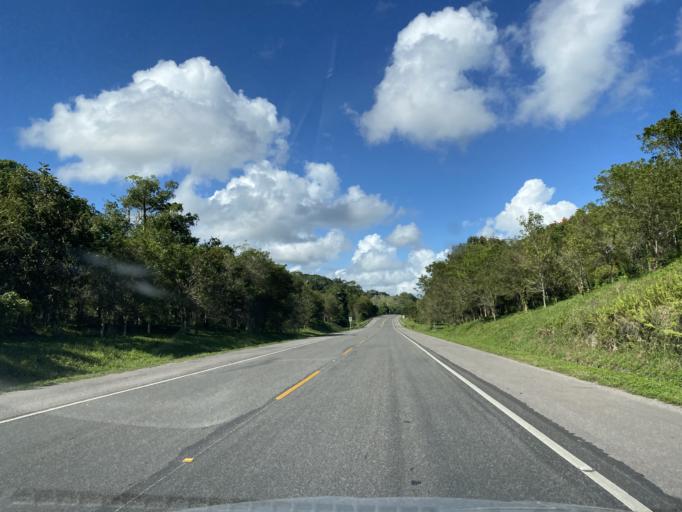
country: DO
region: Monte Plata
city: Majagual
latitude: 19.0297
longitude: -69.8250
